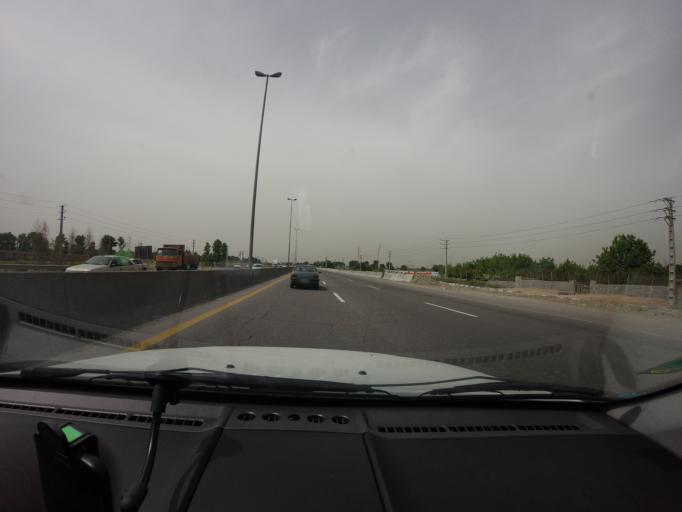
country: IR
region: Tehran
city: Eslamshahr
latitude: 35.5713
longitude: 51.1390
